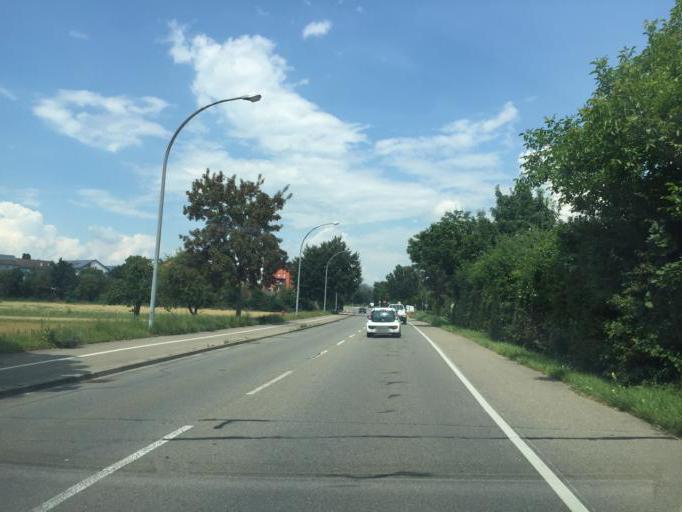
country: DE
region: Baden-Wuerttemberg
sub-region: Freiburg Region
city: Rielasingen-Worblingen
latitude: 47.7394
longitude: 8.8502
